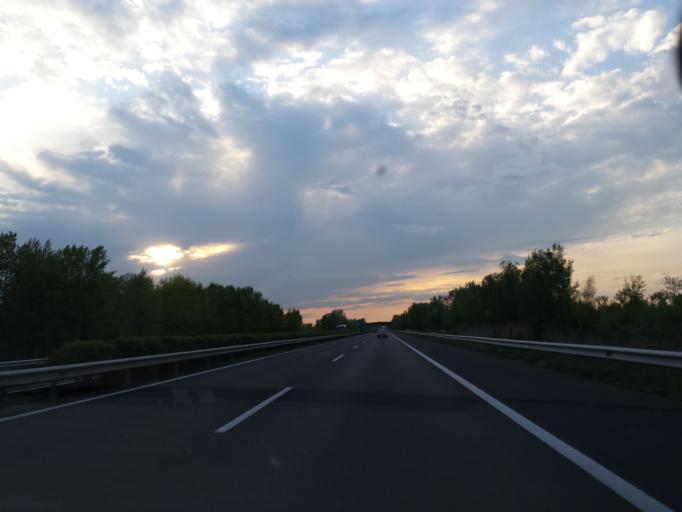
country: HU
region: Gyor-Moson-Sopron
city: Kimle
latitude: 47.7745
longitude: 17.3648
